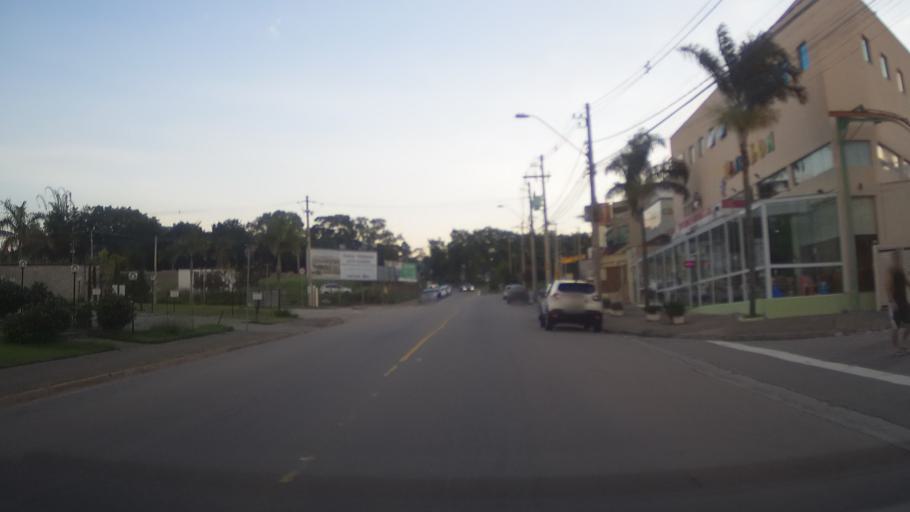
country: BR
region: Sao Paulo
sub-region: Jundiai
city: Jundiai
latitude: -23.1915
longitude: -46.9608
